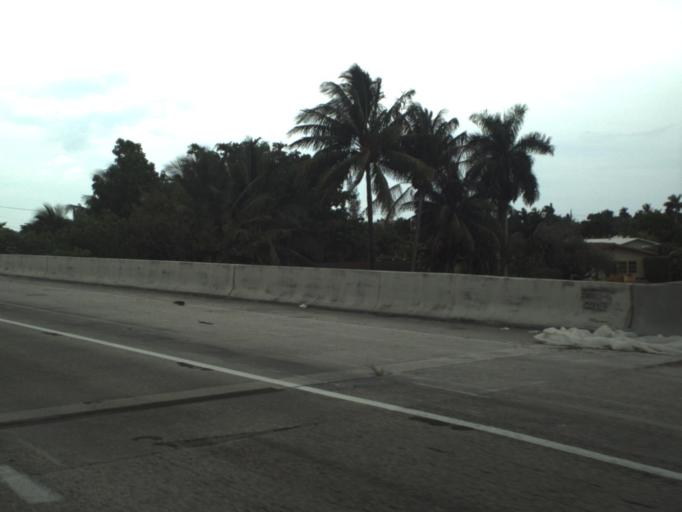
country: US
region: Florida
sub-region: Broward County
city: Hollywood
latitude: 26.0237
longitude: -80.1670
